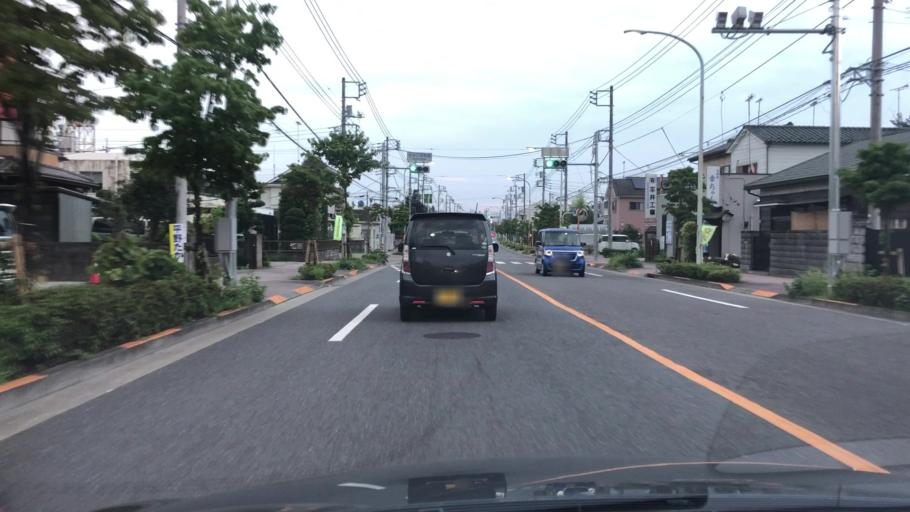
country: JP
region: Tokyo
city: Ome
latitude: 35.7407
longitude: 139.2673
